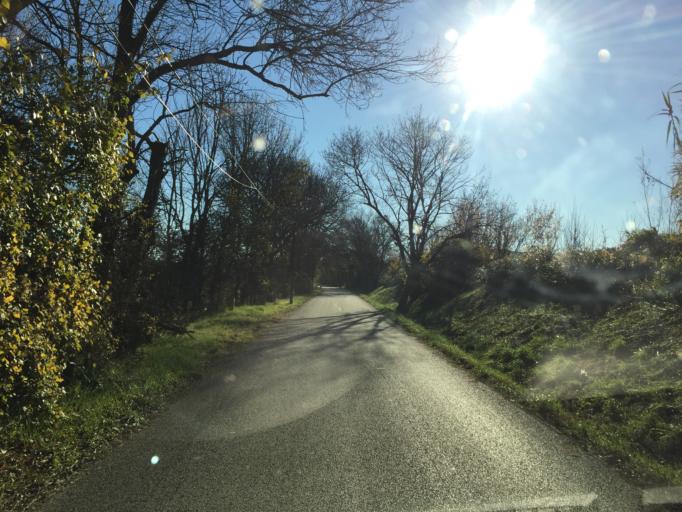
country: FR
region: Provence-Alpes-Cote d'Azur
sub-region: Departement du Vaucluse
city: Bedarrides
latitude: 44.0299
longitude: 4.9018
